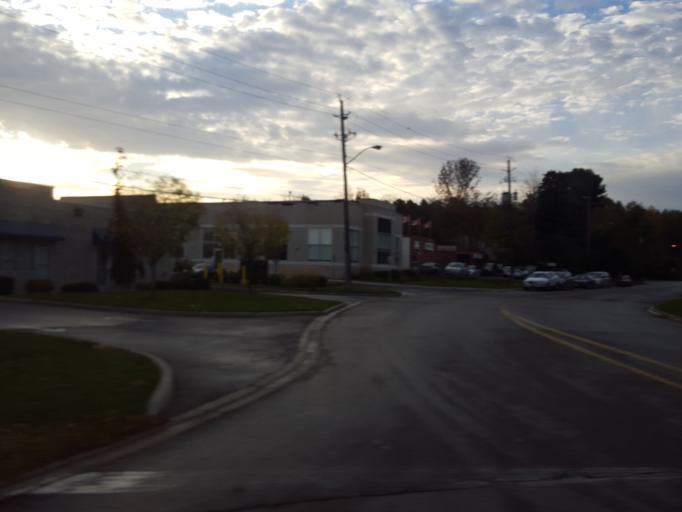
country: CA
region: Ontario
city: Newmarket
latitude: 44.0002
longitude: -79.4564
